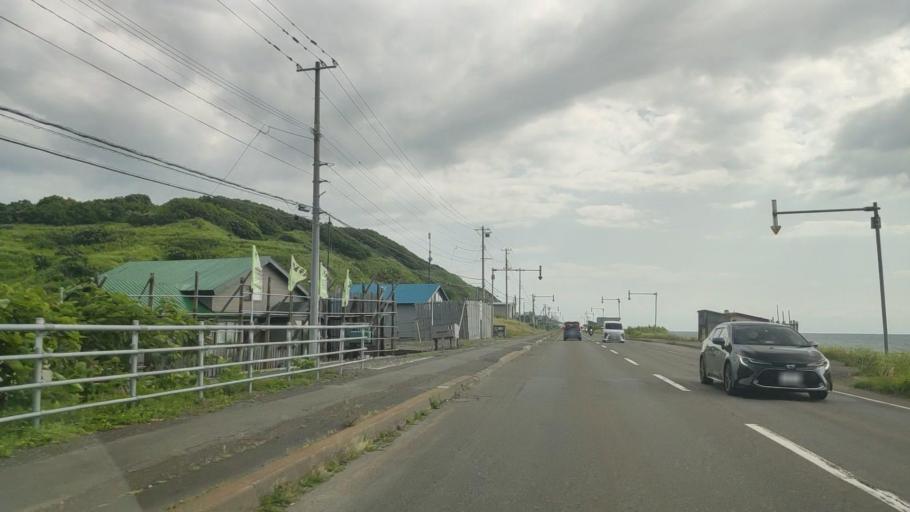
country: JP
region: Hokkaido
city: Rumoi
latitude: 44.1810
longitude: 141.6587
